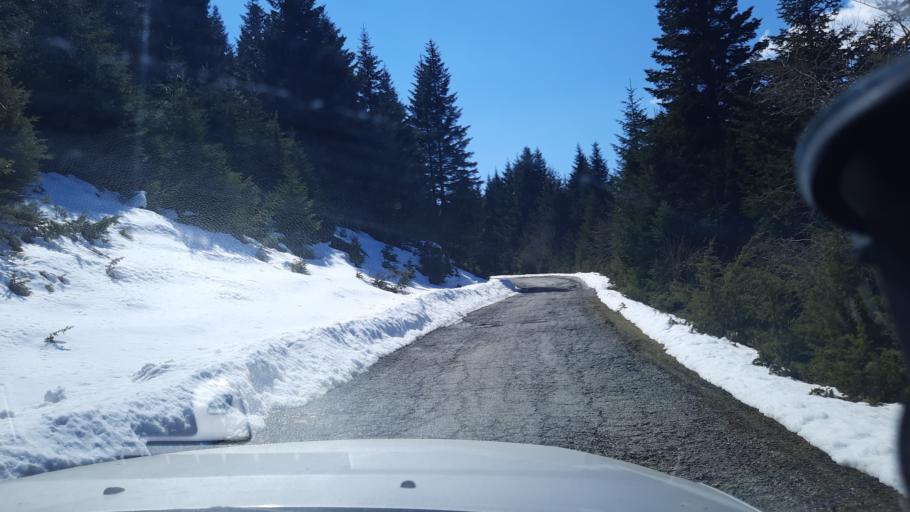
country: MK
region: Gostivar
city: Vrutok
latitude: 41.7185
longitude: 20.7284
